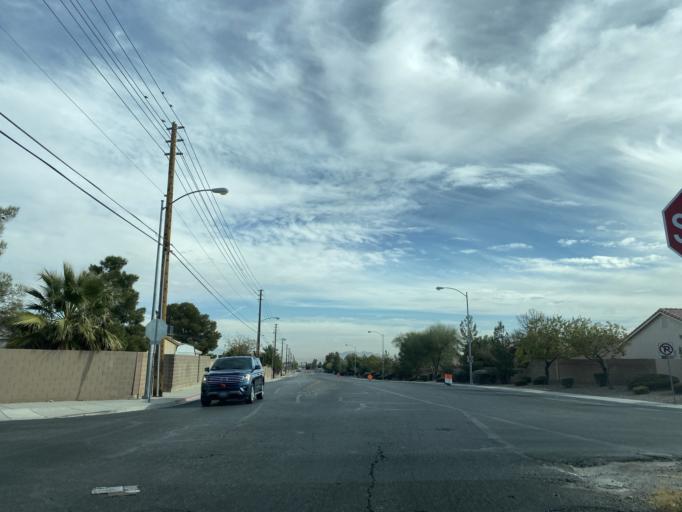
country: US
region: Nevada
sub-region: Clark County
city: North Las Vegas
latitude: 36.2469
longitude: -115.1849
